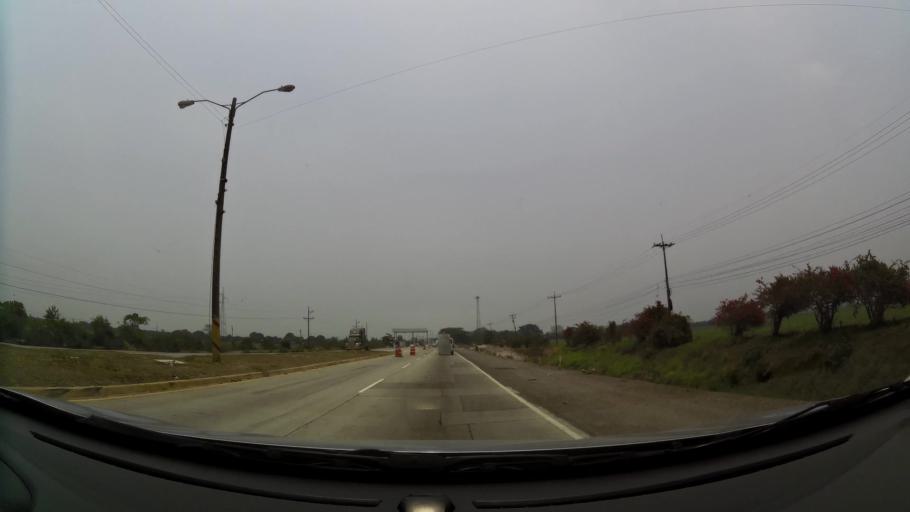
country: HN
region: Yoro
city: El Progreso
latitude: 15.4118
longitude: -87.8558
